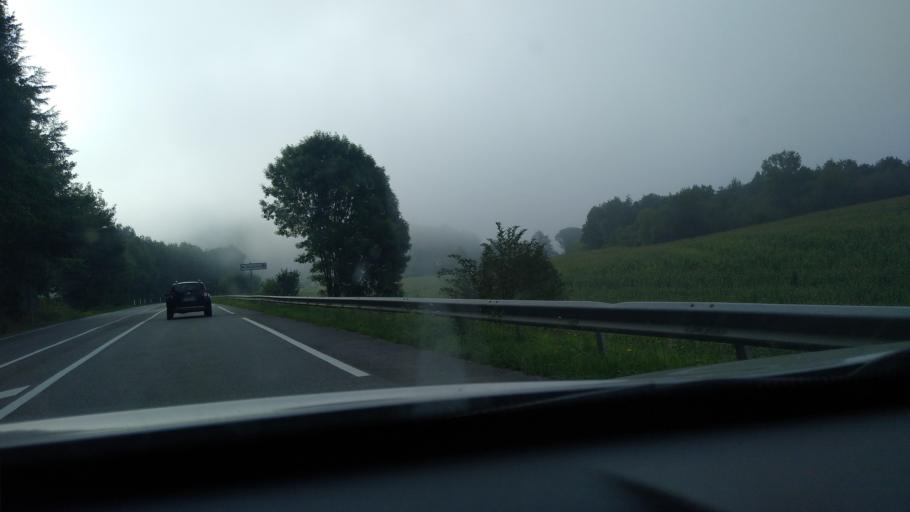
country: FR
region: Midi-Pyrenees
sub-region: Departement de la Haute-Garonne
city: Salies-du-Salat
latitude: 43.1178
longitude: 0.9337
